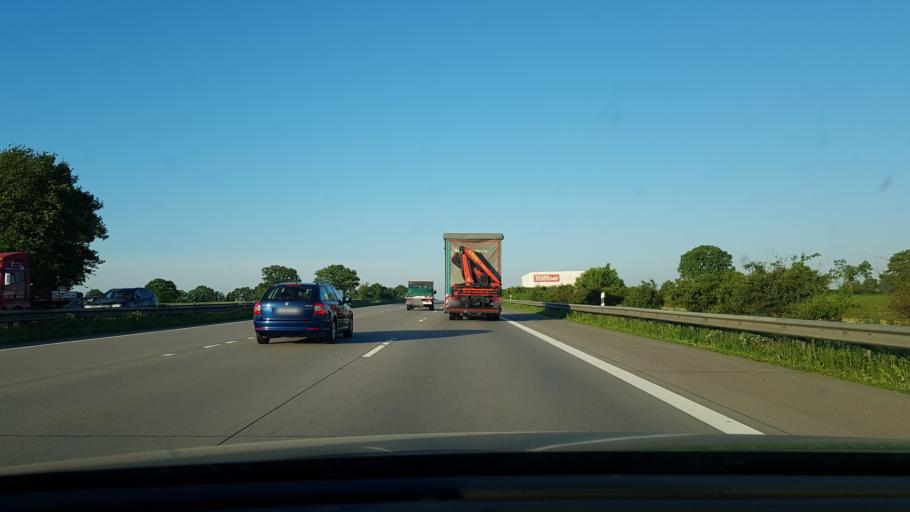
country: DE
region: Schleswig-Holstein
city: Stapelfeld
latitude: 53.5851
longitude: 10.2097
